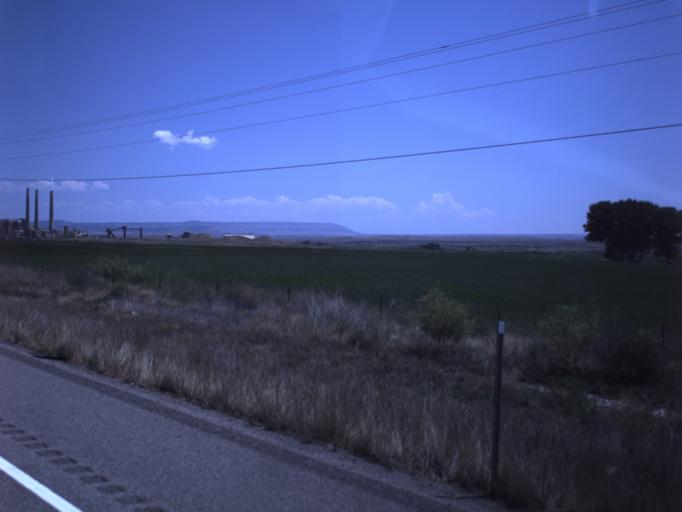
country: US
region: Utah
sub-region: Emery County
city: Orangeville
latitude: 39.1625
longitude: -111.0686
